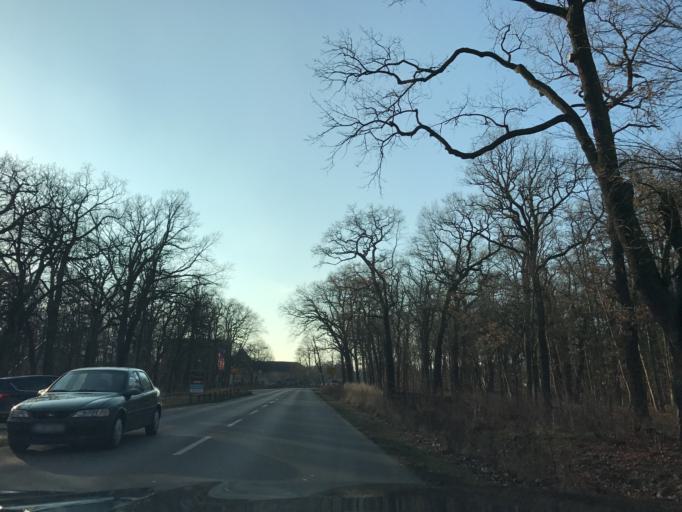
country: DE
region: Brandenburg
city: Brandenburg an der Havel
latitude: 52.3746
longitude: 12.5101
